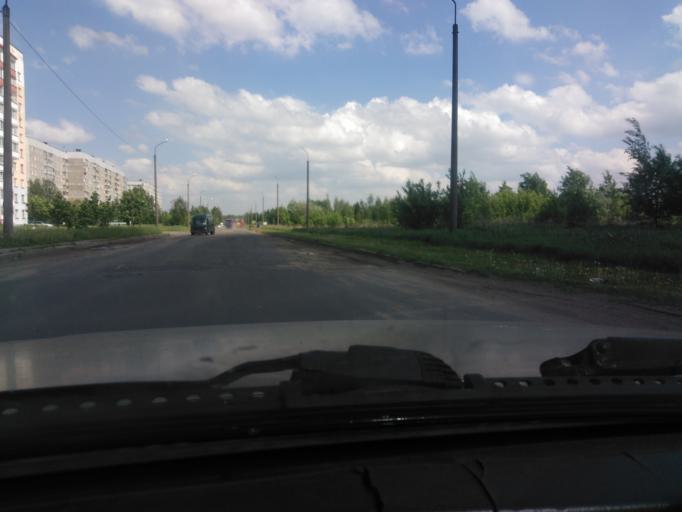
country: BY
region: Mogilev
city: Mahilyow
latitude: 53.9447
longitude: 30.3690
